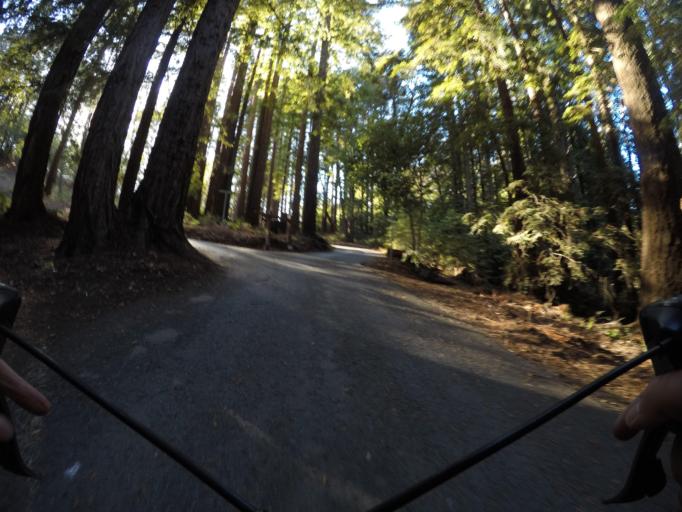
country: US
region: California
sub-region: Santa Cruz County
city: Brookdale
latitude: 37.1097
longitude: -122.0977
